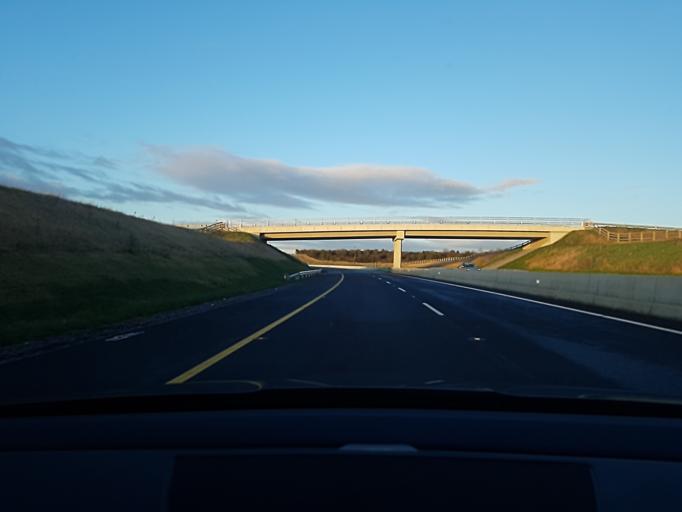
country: IE
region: Connaught
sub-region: County Galway
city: Athenry
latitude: 53.3600
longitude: -8.7896
